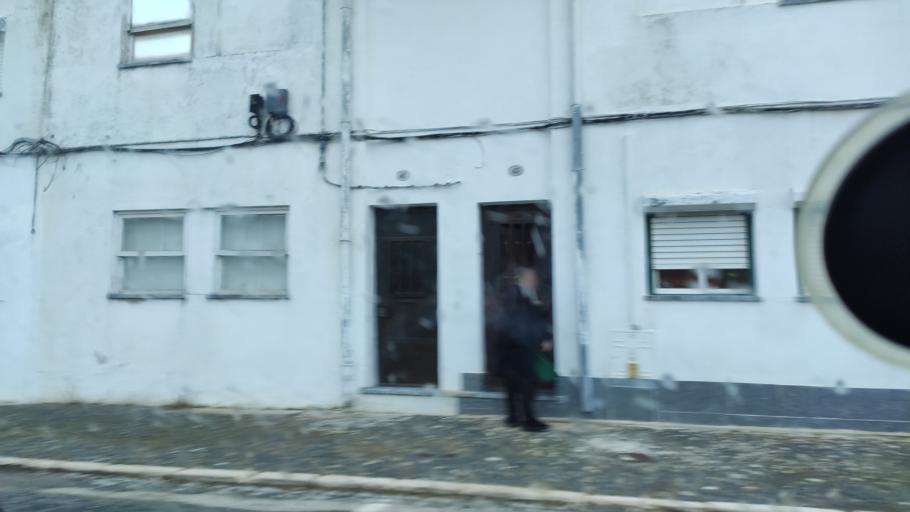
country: PT
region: Beja
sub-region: Beja
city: Beja
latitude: 38.0134
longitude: -7.8495
